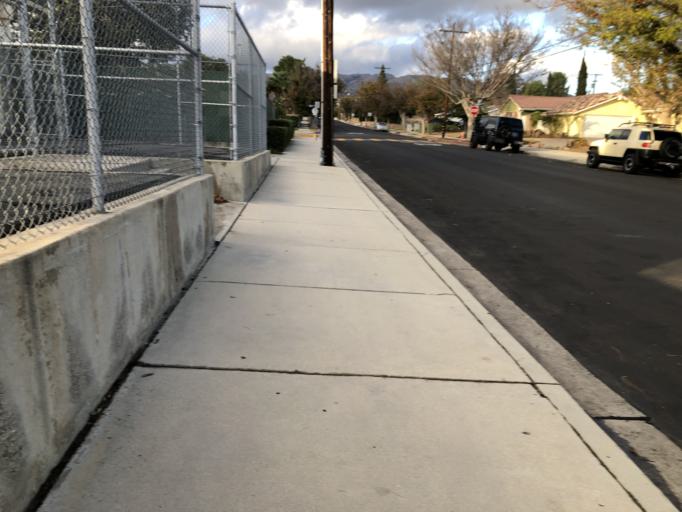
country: US
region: California
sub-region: Los Angeles County
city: Chatsworth
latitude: 34.2621
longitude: -118.5843
